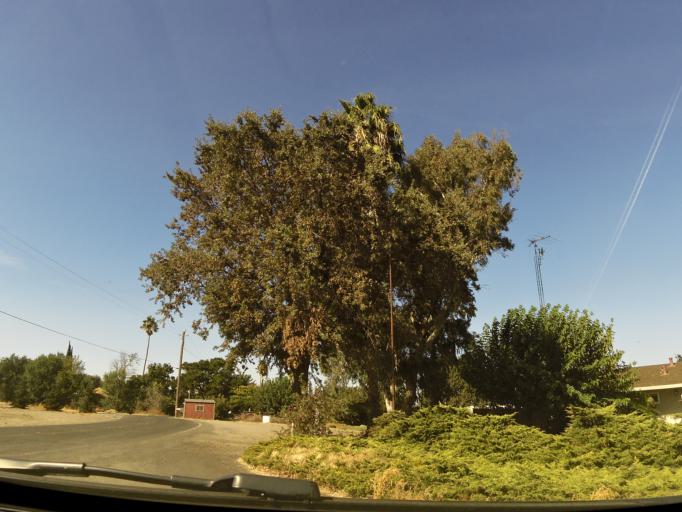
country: US
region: California
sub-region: San Joaquin County
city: Tracy
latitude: 37.7907
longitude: -121.4351
